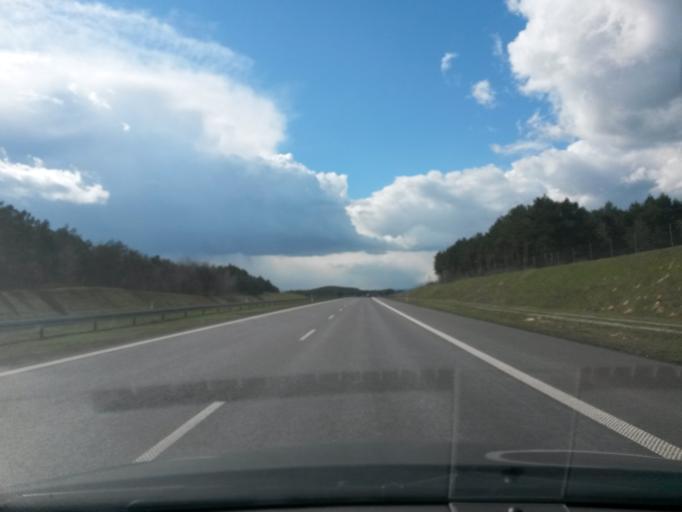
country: PL
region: Greater Poland Voivodeship
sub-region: Powiat kolski
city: Koscielec
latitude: 52.1416
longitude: 18.5489
